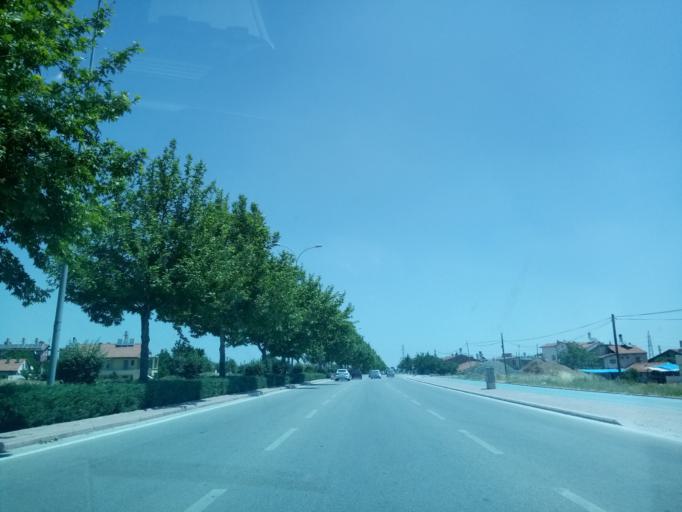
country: TR
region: Konya
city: Meram
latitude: 37.8251
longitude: 32.4677
